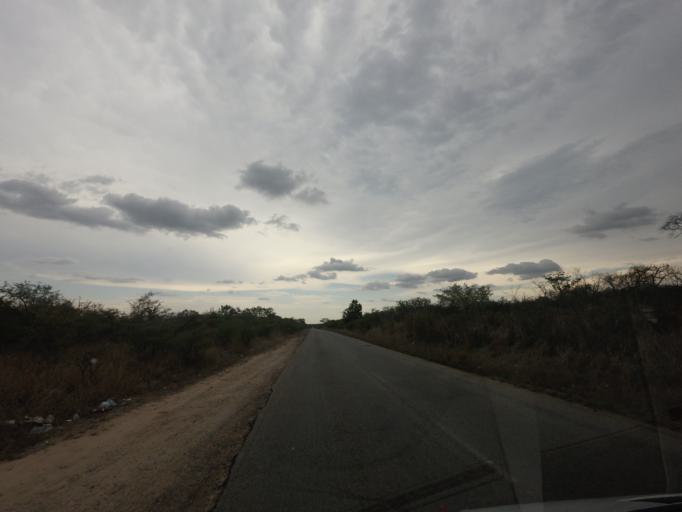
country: ZA
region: Limpopo
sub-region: Mopani District Municipality
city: Hoedspruit
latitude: -24.5282
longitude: 30.9738
